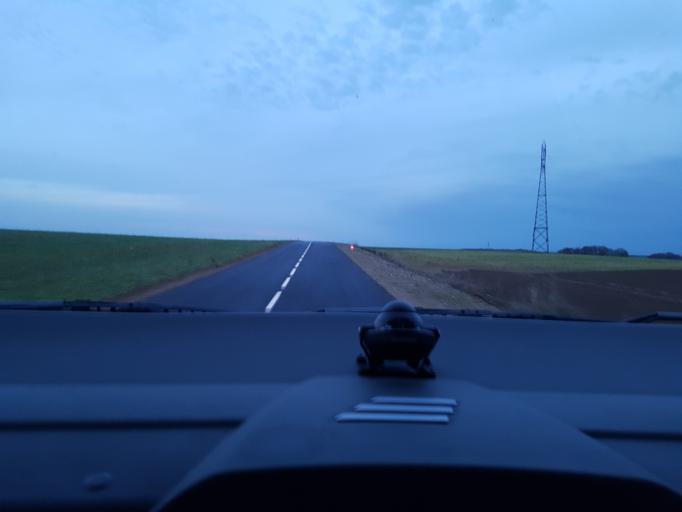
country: FR
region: Picardie
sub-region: Departement de la Somme
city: Beauquesne
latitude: 50.0927
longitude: 2.4325
